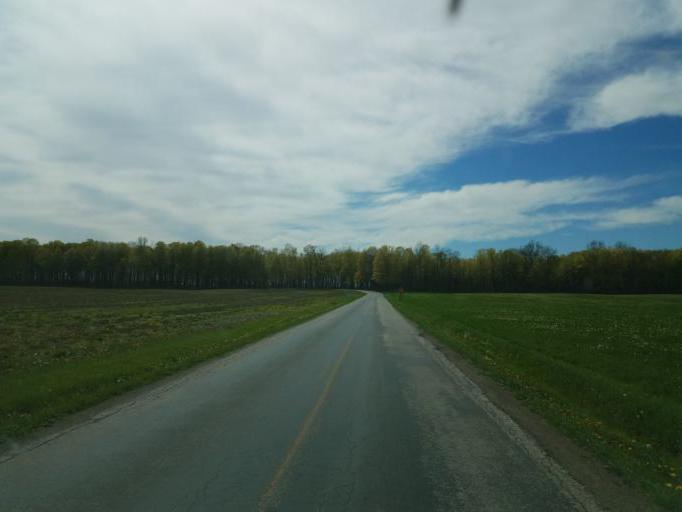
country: US
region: Ohio
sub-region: Richland County
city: Shelby
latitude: 40.9011
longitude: -82.6034
